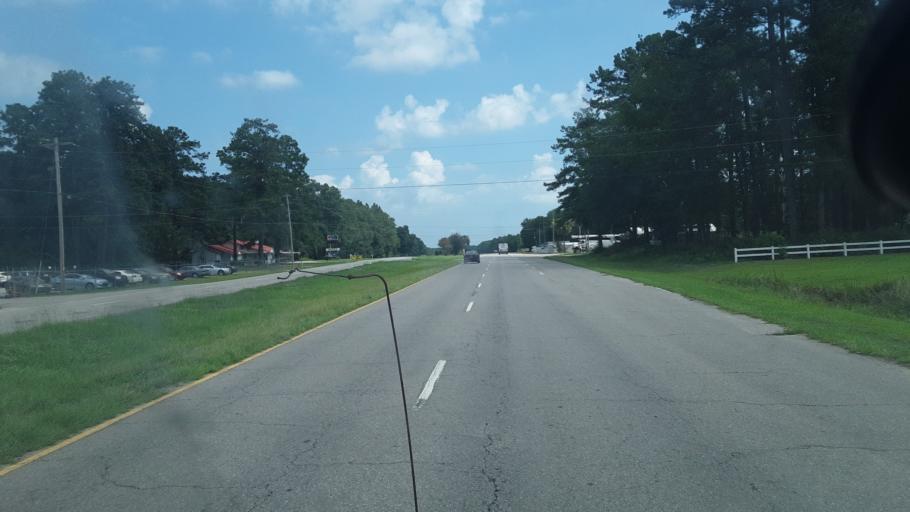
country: US
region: South Carolina
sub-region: Bamberg County
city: Bamberg
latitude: 33.3195
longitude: -81.0312
